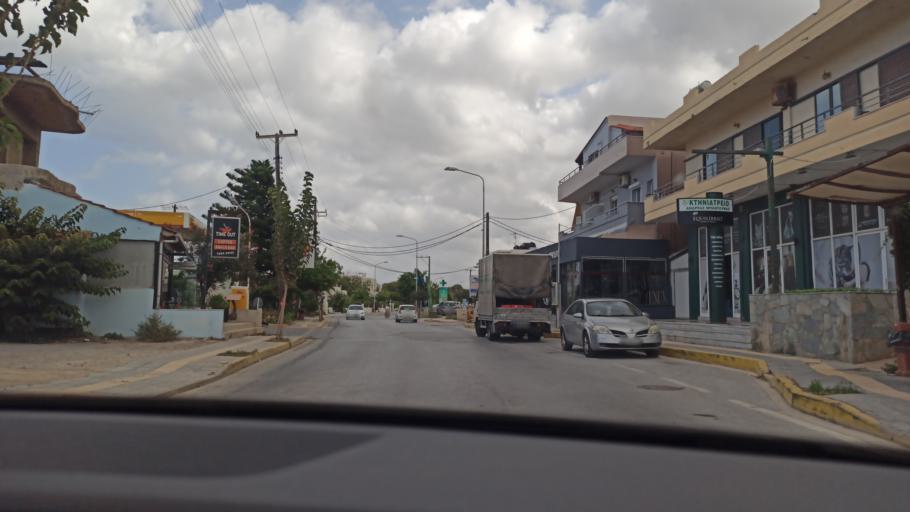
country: GR
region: Crete
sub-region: Nomos Irakleiou
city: Gazi
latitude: 35.3350
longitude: 25.0910
